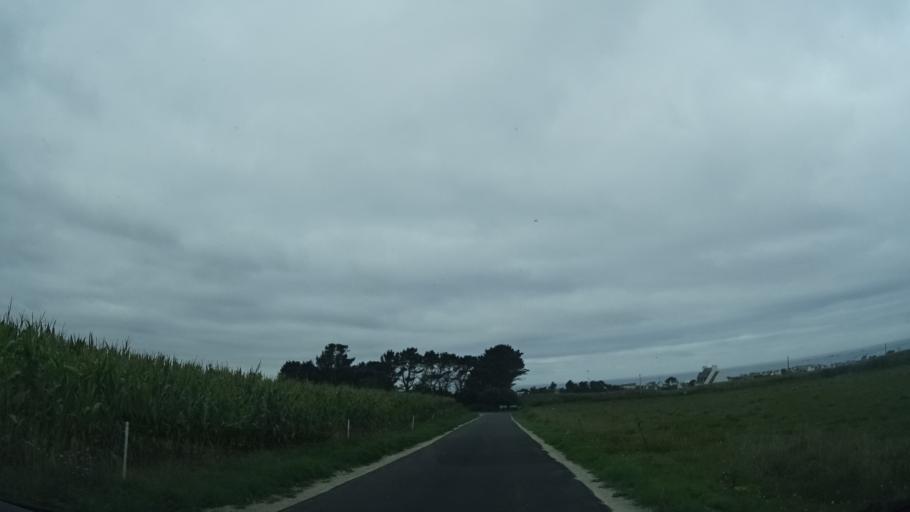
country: FR
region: Brittany
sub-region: Departement du Finistere
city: Lampaul-Plouarzel
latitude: 48.4588
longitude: -4.7514
